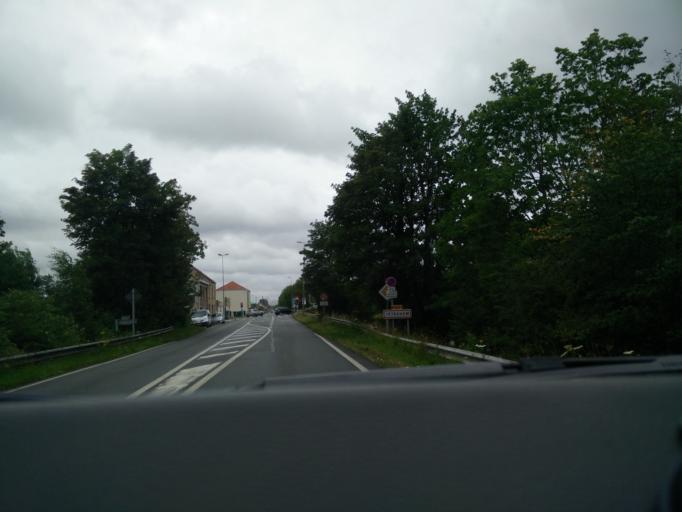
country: FR
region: Nord-Pas-de-Calais
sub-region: Departement du Nord
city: Coudekerque-Branche
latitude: 51.0374
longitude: 2.4163
